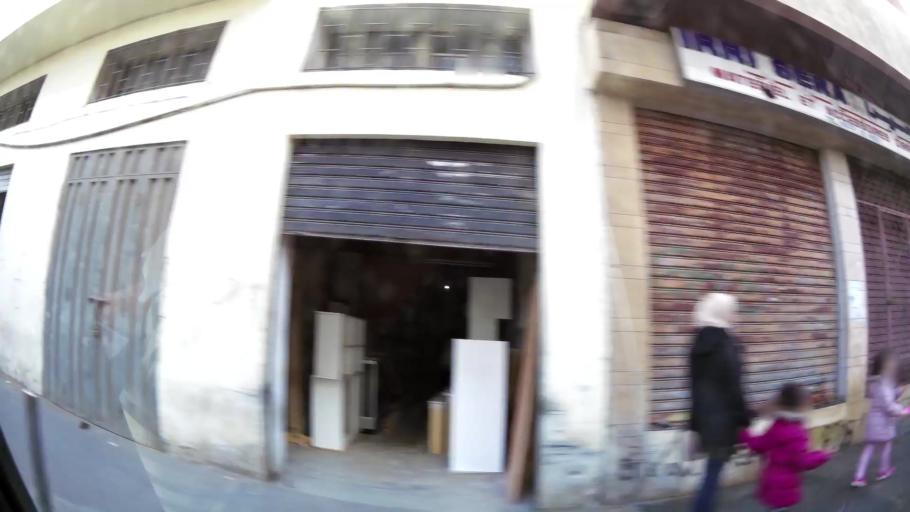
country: MA
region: Grand Casablanca
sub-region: Casablanca
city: Casablanca
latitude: 33.5944
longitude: -7.5869
